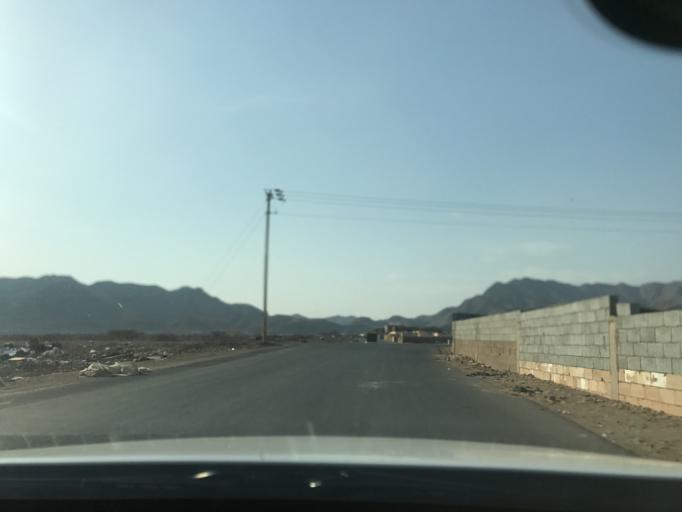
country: SA
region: Makkah
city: Al Jumum
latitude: 21.4411
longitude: 39.5157
